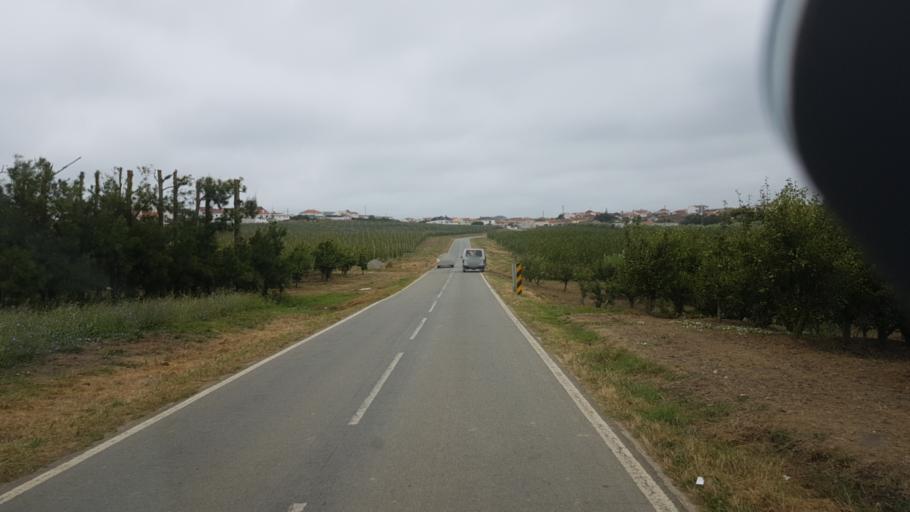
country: PT
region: Leiria
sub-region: Bombarral
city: Bombarral
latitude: 39.2860
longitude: -9.1963
